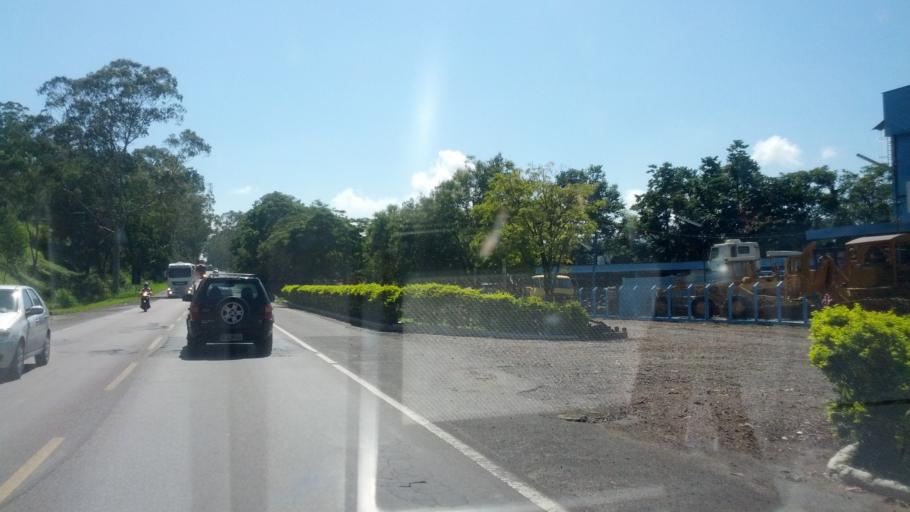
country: BR
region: Santa Catarina
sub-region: Rio Do Sul
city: Rio do Sul
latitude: -27.1890
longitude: -49.6161
